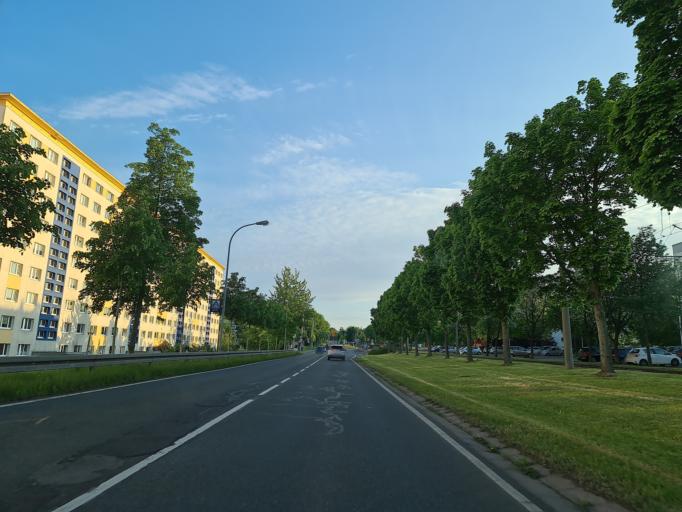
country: DE
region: Saxony
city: Neukirchen
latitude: 50.8067
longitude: 12.8905
